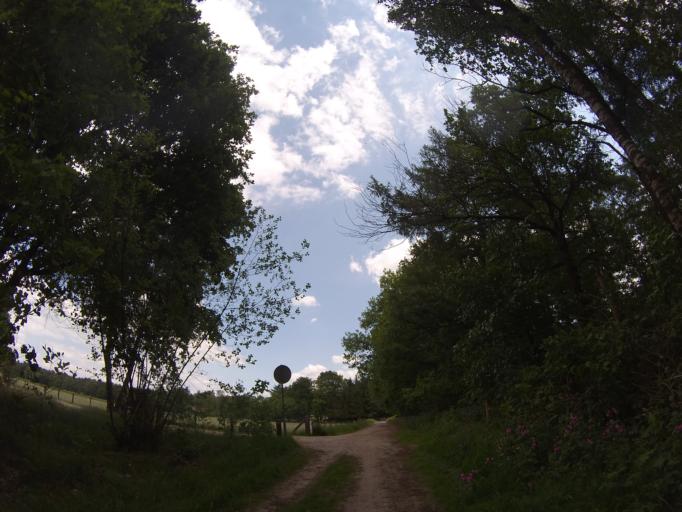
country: NL
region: Gelderland
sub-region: Gemeente Barneveld
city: Garderen
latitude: 52.2324
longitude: 5.6928
